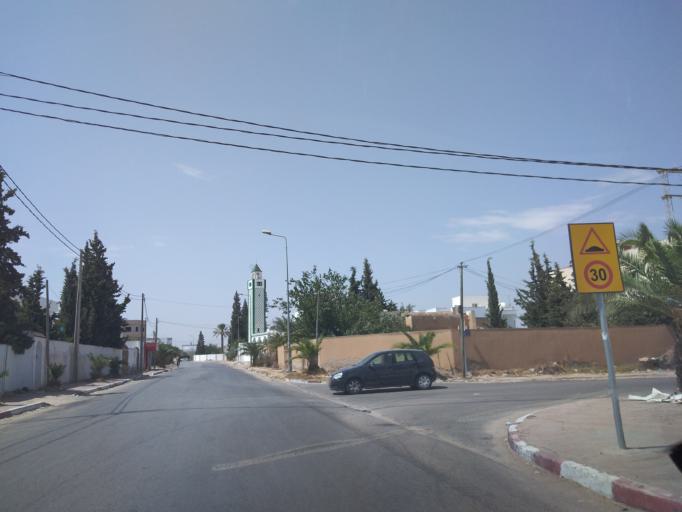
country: TN
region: Safaqis
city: Sfax
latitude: 34.7613
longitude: 10.7487
